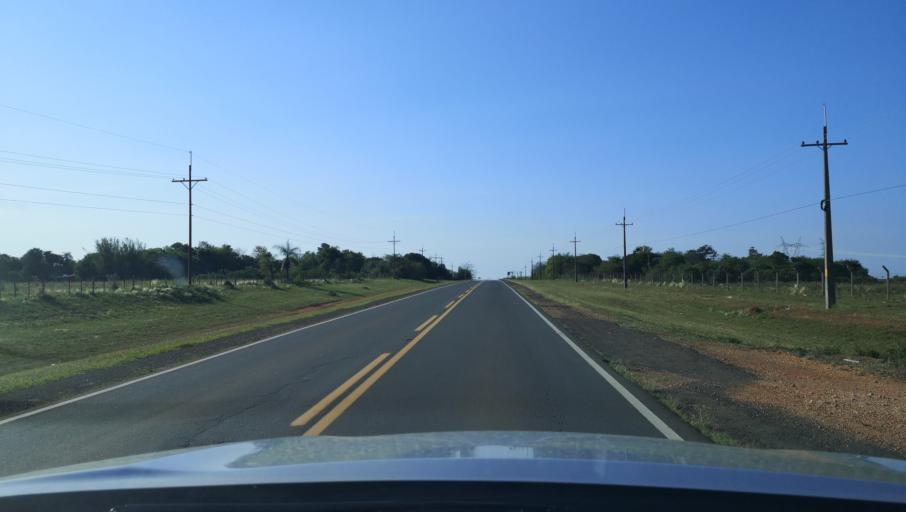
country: PY
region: Misiones
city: Santa Maria
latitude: -26.8019
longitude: -57.0213
